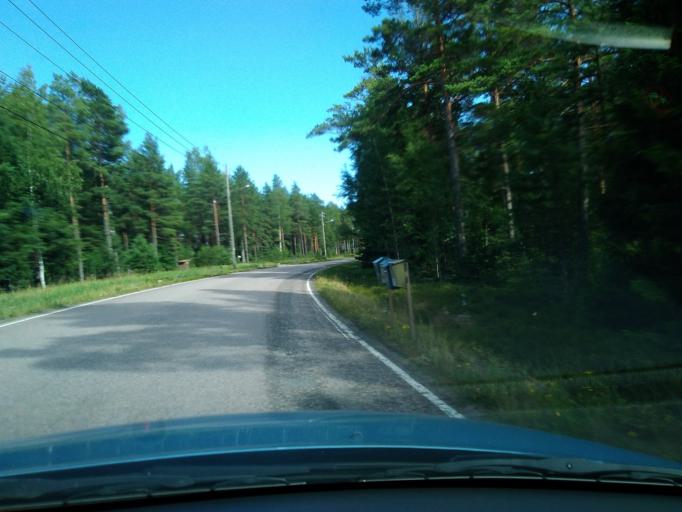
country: FI
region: Uusimaa
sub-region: Raaseporin
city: Hanko
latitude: 59.8375
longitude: 23.1004
